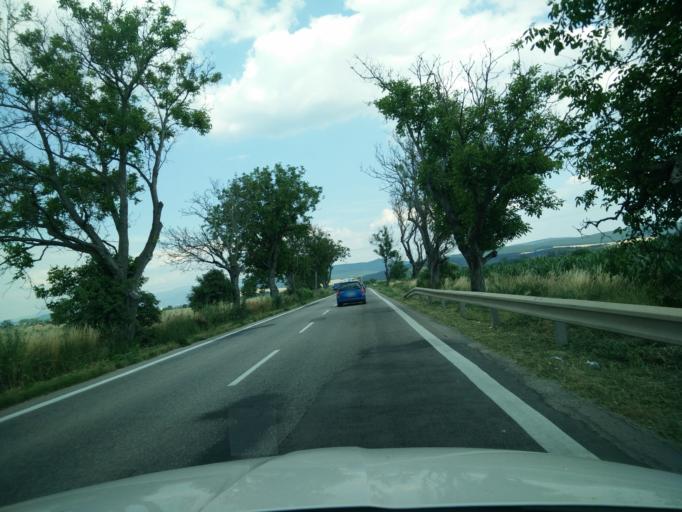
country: SK
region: Nitriansky
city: Partizanske
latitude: 48.6152
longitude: 18.2791
